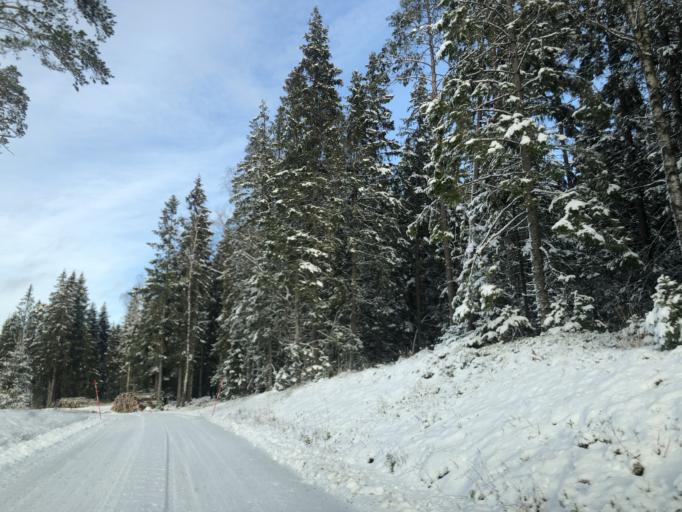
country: SE
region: Vaestra Goetaland
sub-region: Ulricehamns Kommun
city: Ulricehamn
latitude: 57.7576
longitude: 13.5184
